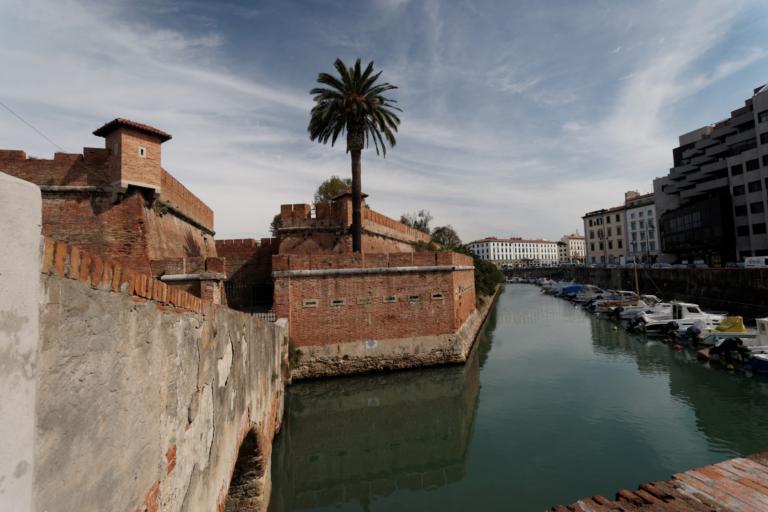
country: IT
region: Tuscany
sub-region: Provincia di Livorno
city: Livorno
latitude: 43.5535
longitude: 10.3109
